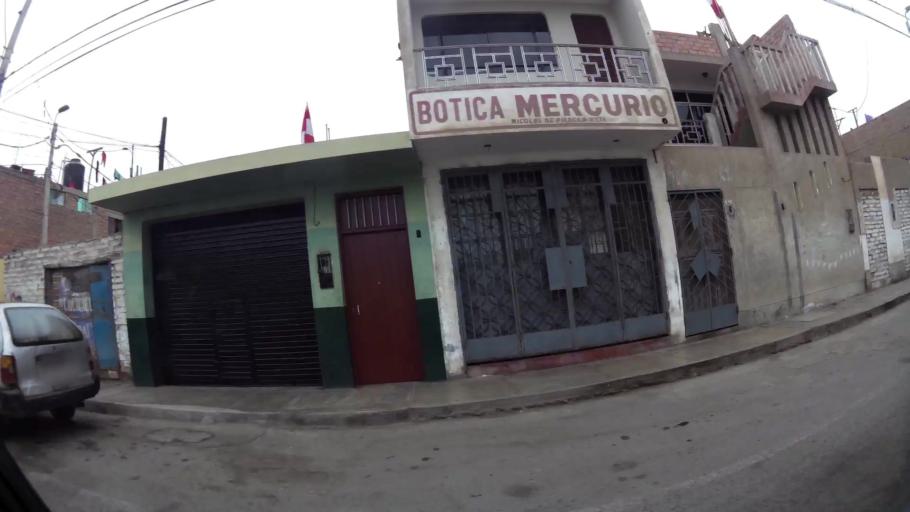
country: PE
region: Lima
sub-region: Barranca
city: Barranca
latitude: -10.7527
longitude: -77.7652
